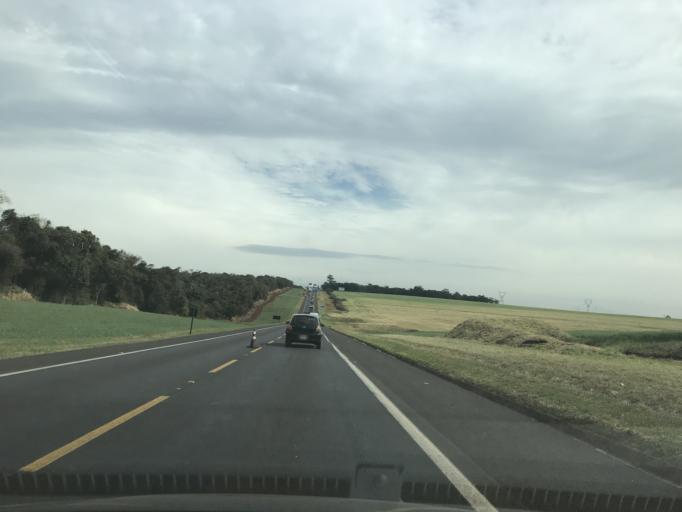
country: BR
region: Parana
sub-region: Cascavel
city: Cascavel
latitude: -25.0792
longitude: -53.7013
